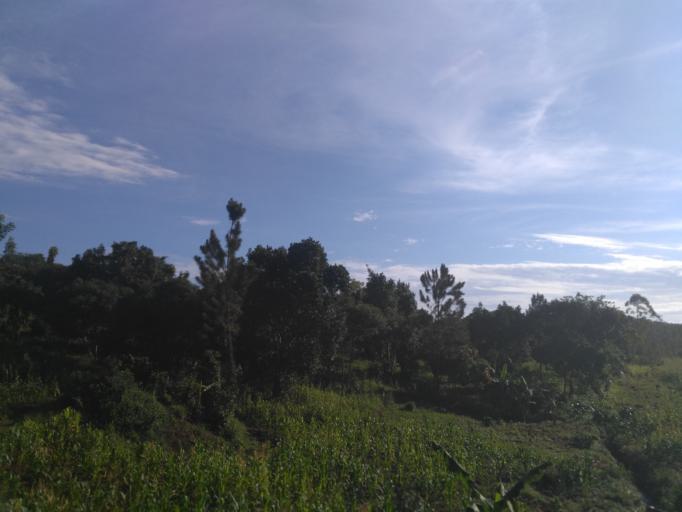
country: UG
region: Eastern Region
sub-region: Jinja District
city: Jinja
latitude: 0.4636
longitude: 33.1815
